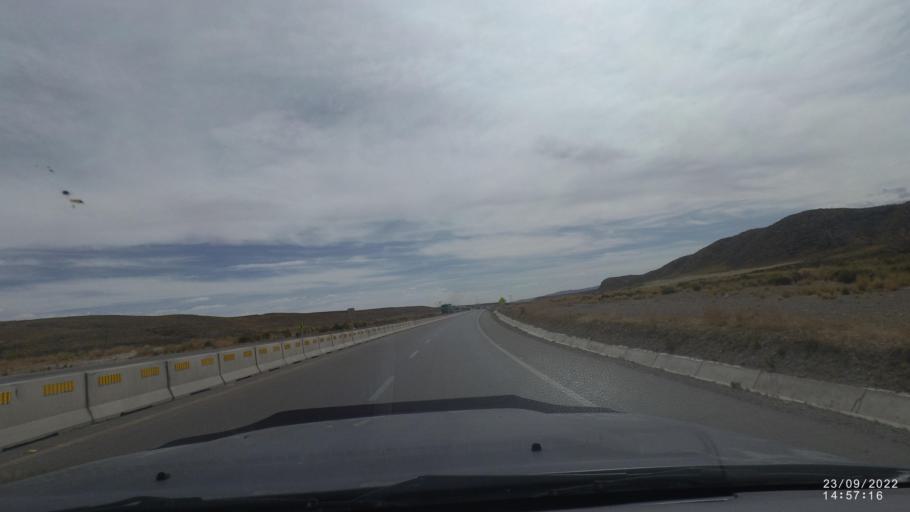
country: BO
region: La Paz
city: Colquiri
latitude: -17.6641
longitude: -67.0169
